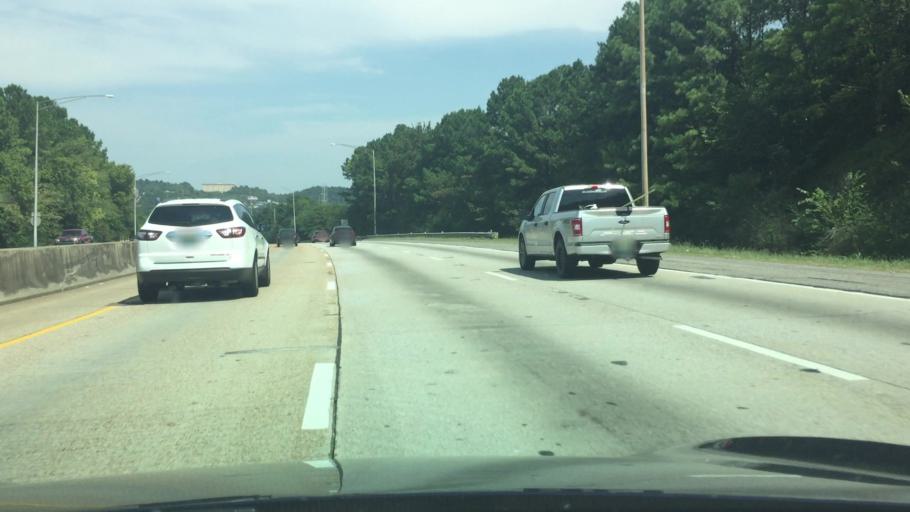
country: US
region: Alabama
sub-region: Jefferson County
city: Homewood
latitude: 33.4570
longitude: -86.8195
